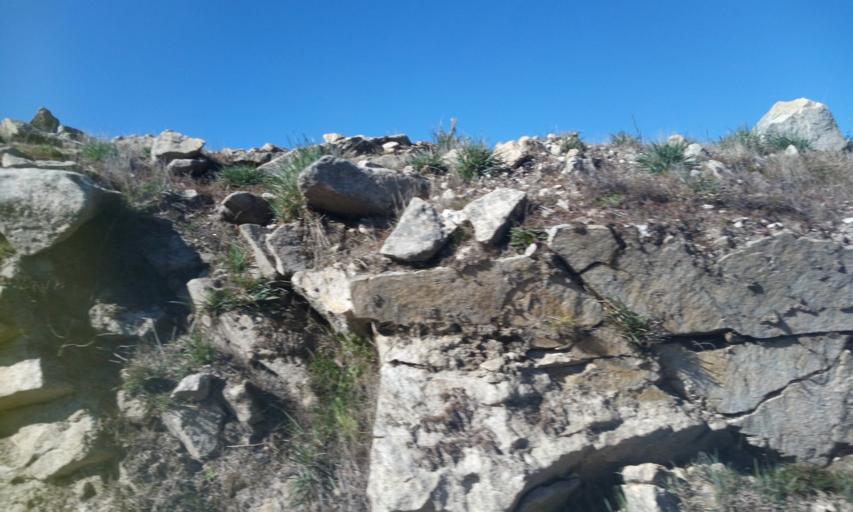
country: PT
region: Guarda
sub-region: Manteigas
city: Manteigas
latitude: 40.4978
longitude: -7.5216
